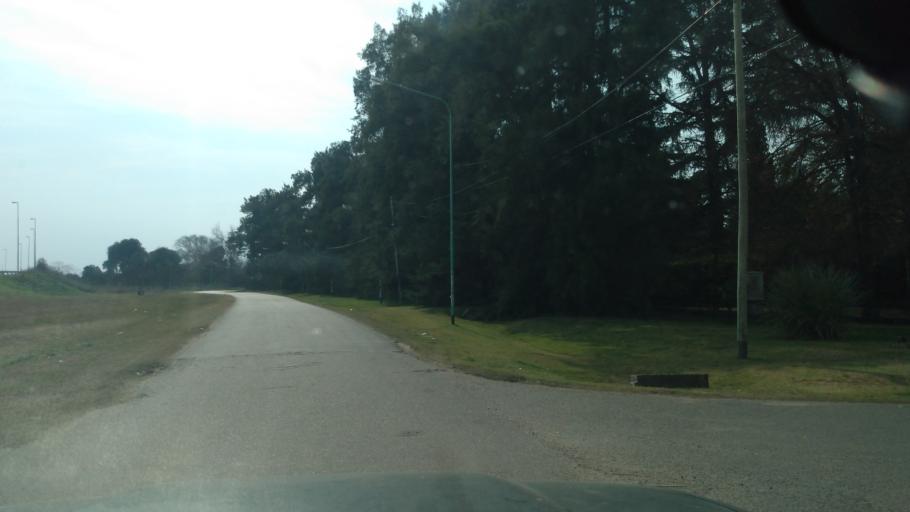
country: AR
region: Buenos Aires
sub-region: Partido de Lujan
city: Lujan
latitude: -34.4952
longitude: -59.0844
